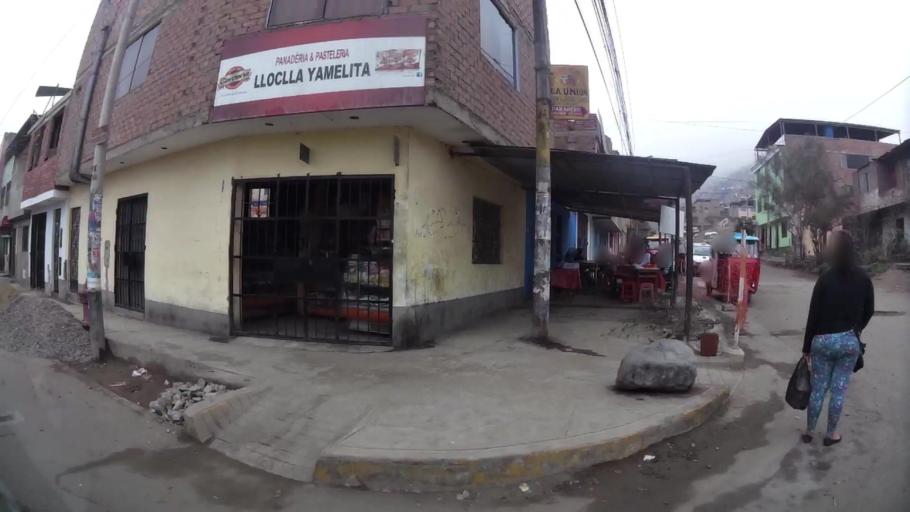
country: PE
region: Lima
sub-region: Lima
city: Surco
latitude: -12.1574
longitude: -76.9527
